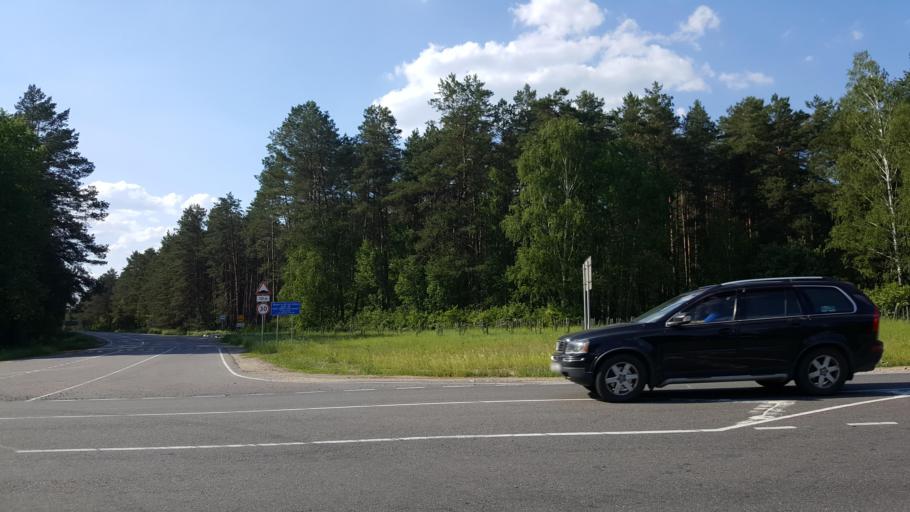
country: BY
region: Brest
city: Zhabinka
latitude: 52.3795
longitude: 24.1227
